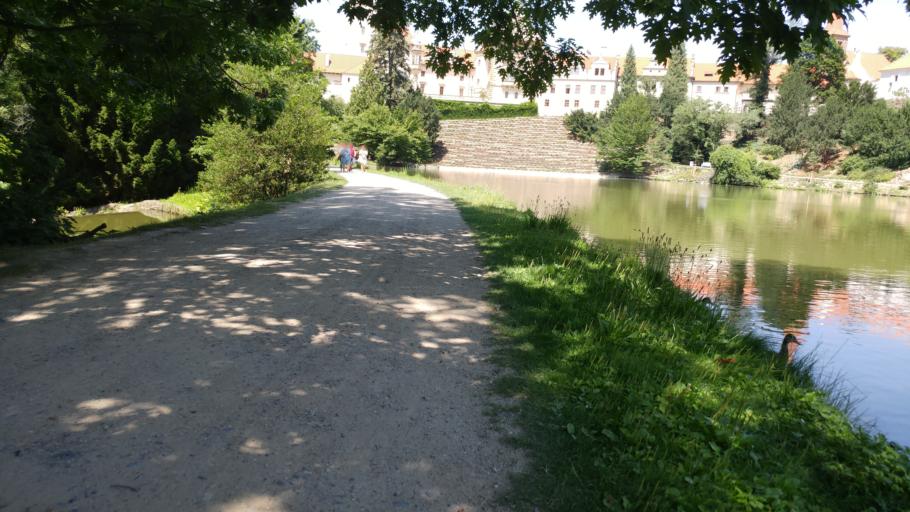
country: CZ
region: Central Bohemia
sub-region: Okres Praha-Zapad
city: Pruhonice
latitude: 49.9991
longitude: 14.5582
